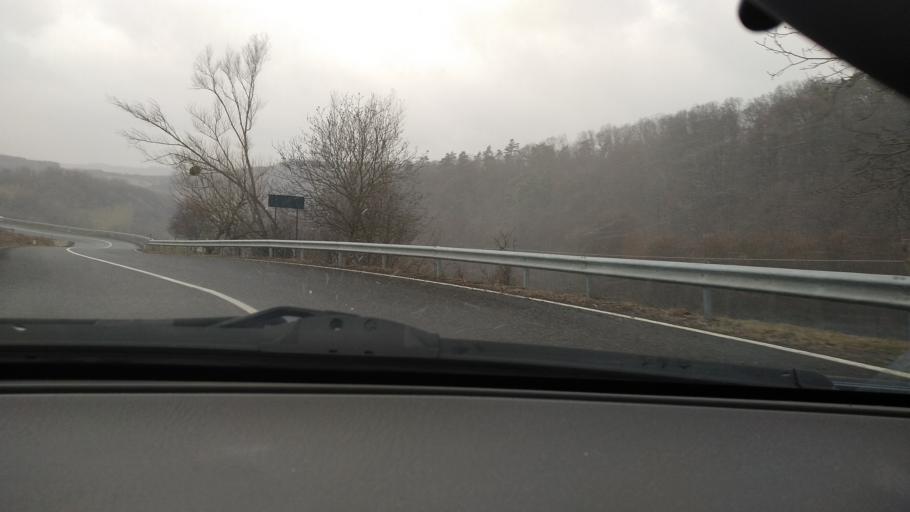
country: RO
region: Mures
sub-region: Comuna Chibed
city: Chibed
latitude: 46.5818
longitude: 24.9521
